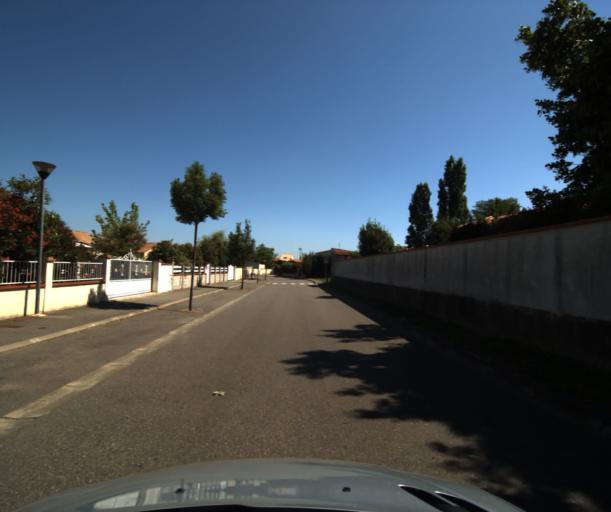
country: FR
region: Midi-Pyrenees
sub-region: Departement de la Haute-Garonne
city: Roquettes
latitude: 43.4983
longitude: 1.3717
